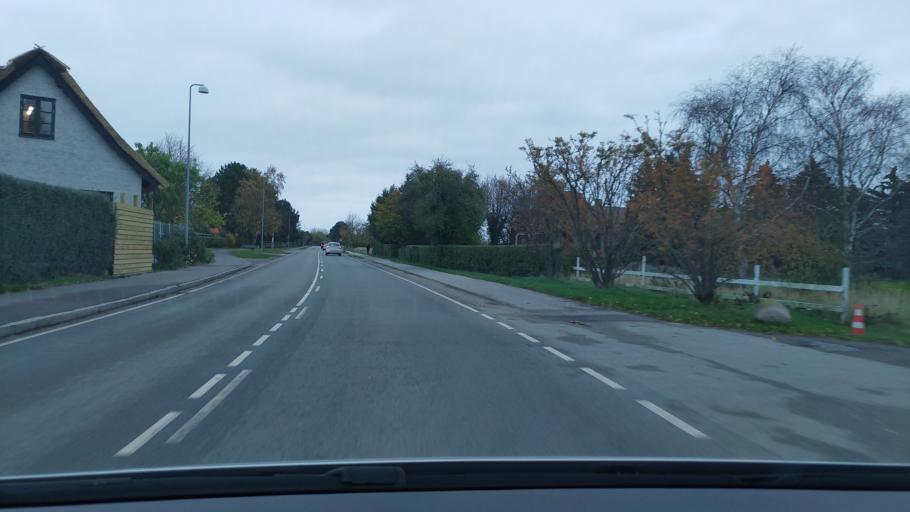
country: DK
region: Capital Region
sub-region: Tarnby Kommune
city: Tarnby
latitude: 55.6102
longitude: 12.6173
